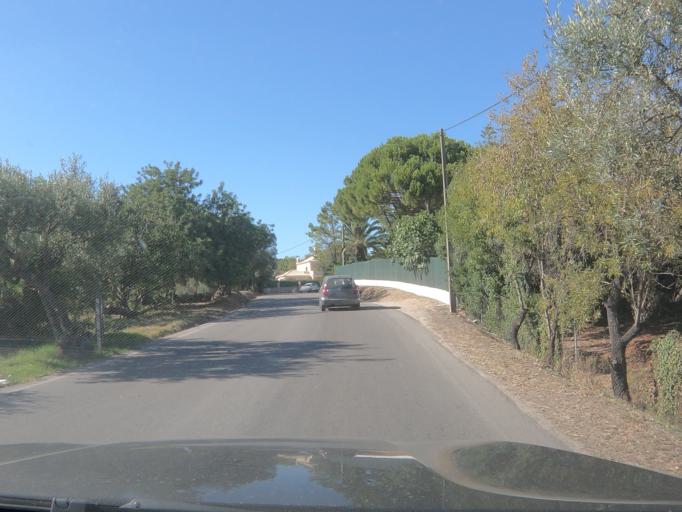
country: PT
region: Faro
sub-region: Loule
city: Almancil
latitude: 37.1087
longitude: -8.0343
